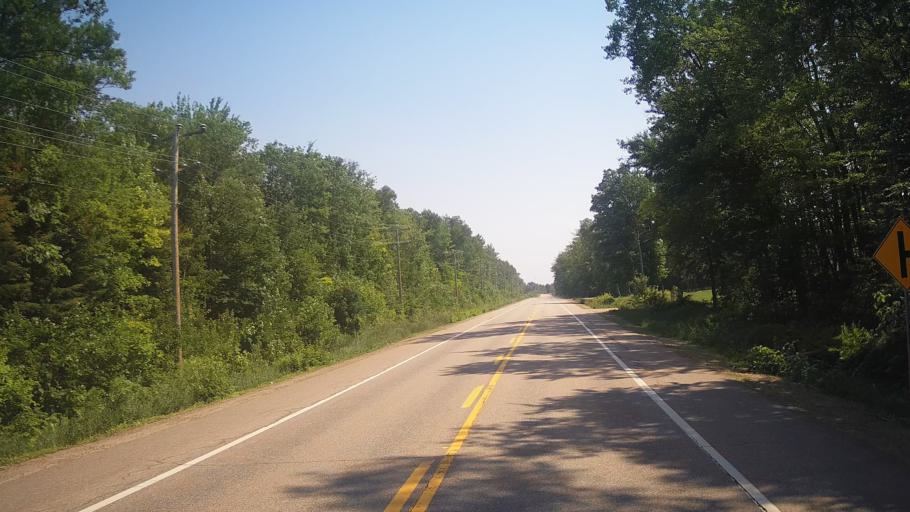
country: CA
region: Ontario
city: Pembroke
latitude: 45.8390
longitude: -77.0134
